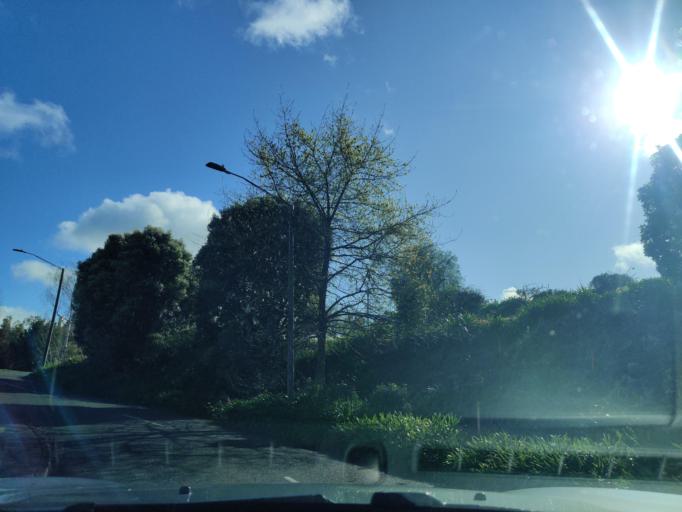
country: NZ
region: Hawke's Bay
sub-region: Hastings District
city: Hastings
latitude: -39.6739
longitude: 176.8946
